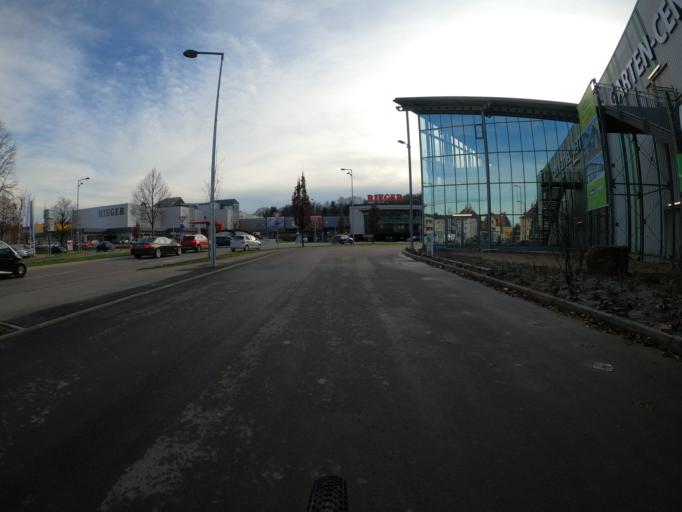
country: DE
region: Baden-Wuerttemberg
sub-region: Regierungsbezirk Stuttgart
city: Goeppingen
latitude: 48.6943
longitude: 9.6648
